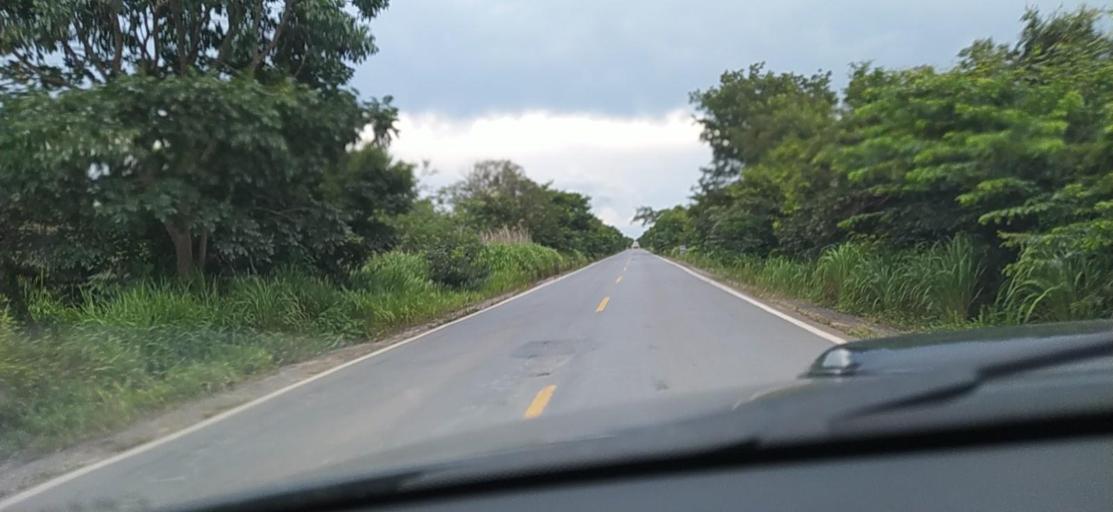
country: BR
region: Minas Gerais
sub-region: Francisco Sa
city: Francisco Sa
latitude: -16.2486
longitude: -43.6299
